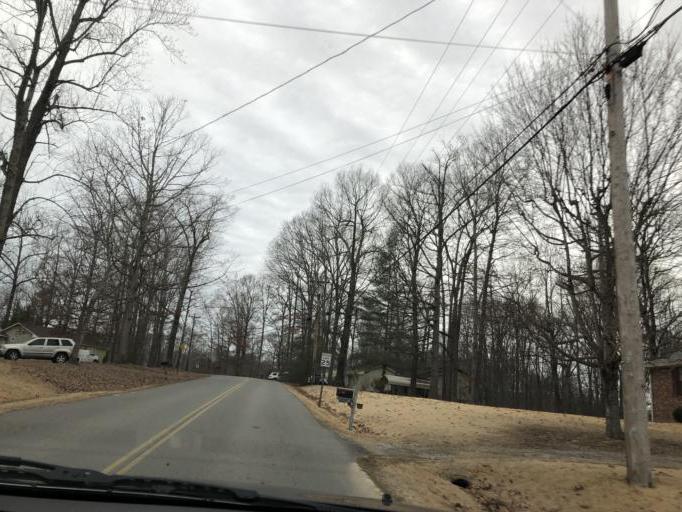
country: US
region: Tennessee
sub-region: Sumner County
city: White House
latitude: 36.4193
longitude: -86.6647
